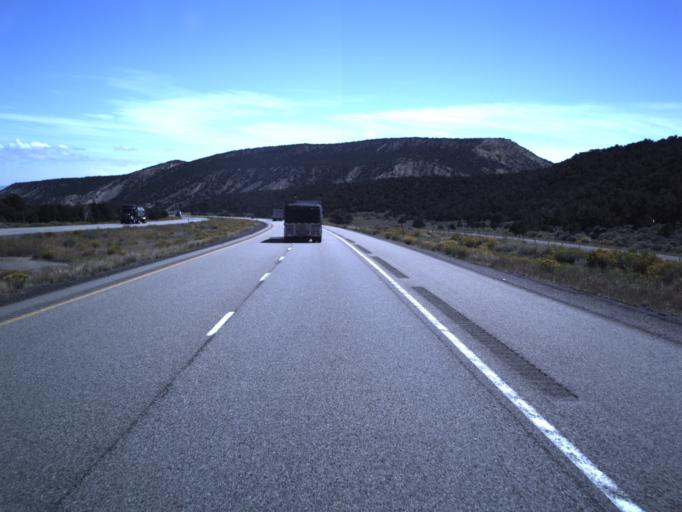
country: US
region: Utah
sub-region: Emery County
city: Ferron
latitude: 38.7555
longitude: -111.3965
